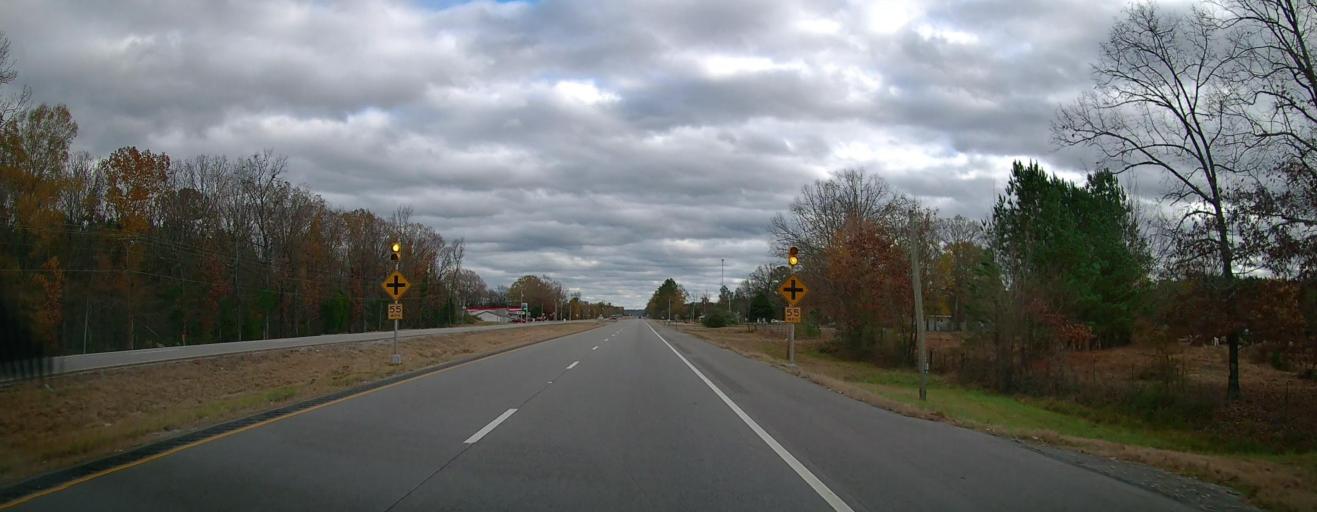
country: US
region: Alabama
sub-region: Lawrence County
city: Town Creek
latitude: 34.6554
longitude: -87.5326
